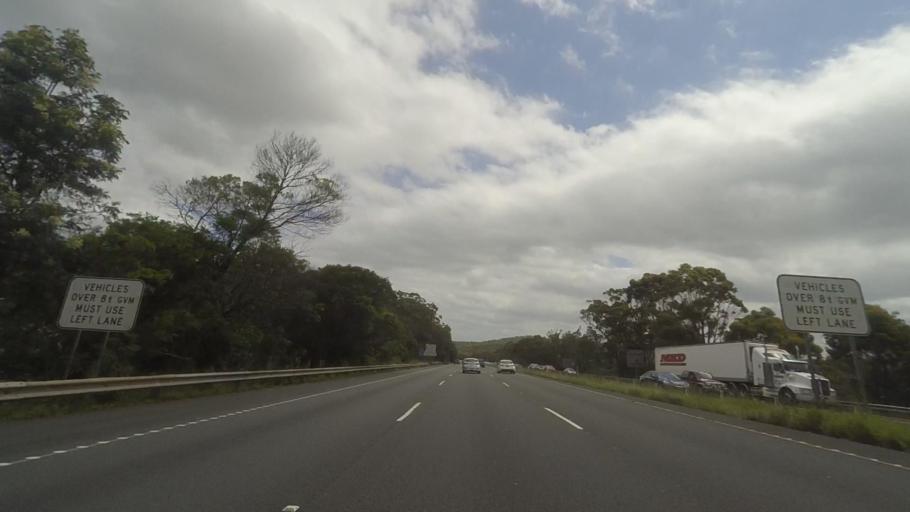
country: AU
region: New South Wales
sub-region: Gosford Shire
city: Point Clare
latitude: -33.4350
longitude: 151.2215
